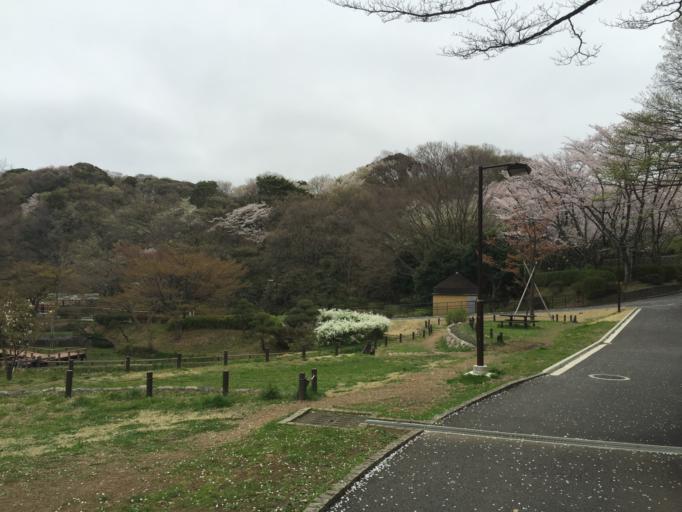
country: JP
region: Kanagawa
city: Yokohama
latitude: 35.4058
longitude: 139.6061
